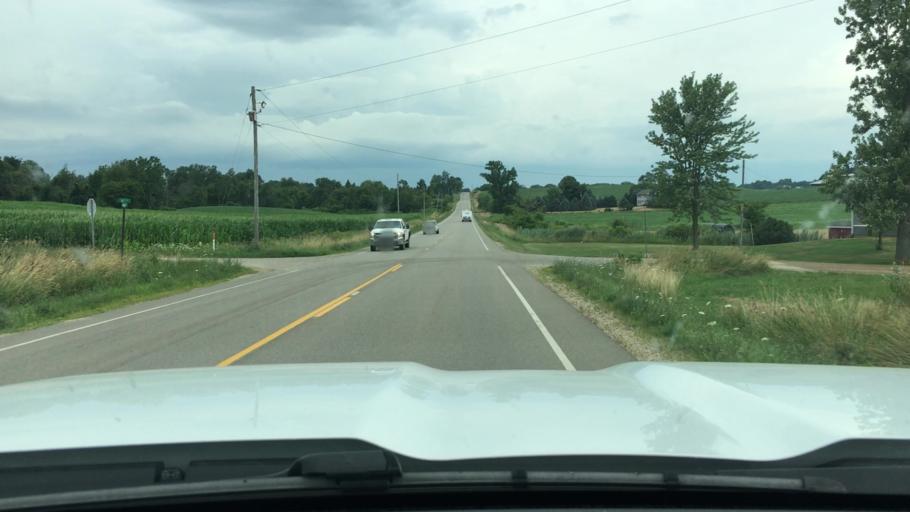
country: US
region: Michigan
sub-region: Ottawa County
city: Hudsonville
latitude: 42.7823
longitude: -85.8216
